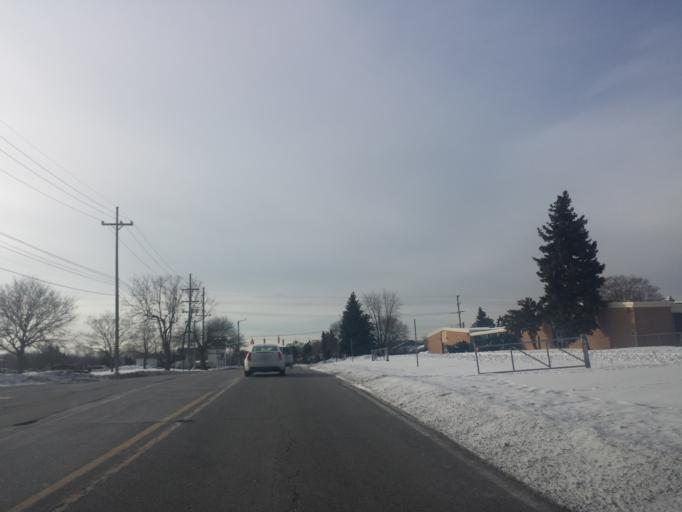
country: US
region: Michigan
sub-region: Oakland County
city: Franklin
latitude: 42.5304
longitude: -83.3406
